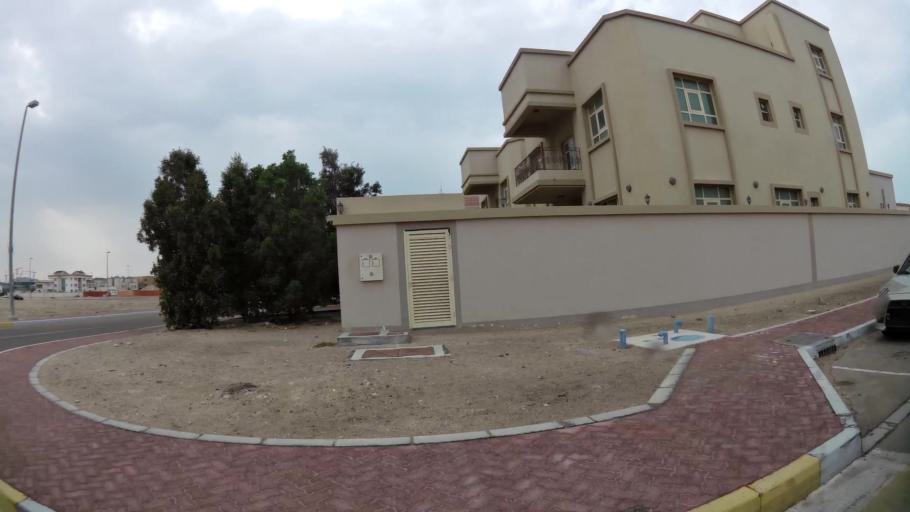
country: AE
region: Abu Dhabi
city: Abu Dhabi
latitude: 24.4316
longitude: 54.4458
